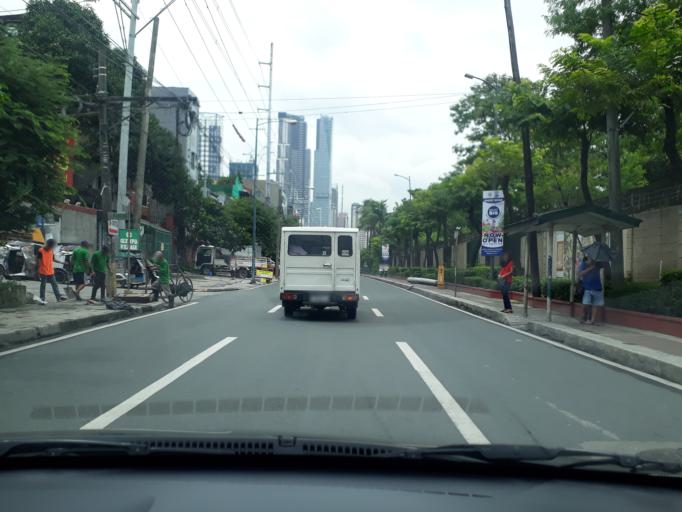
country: PH
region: Metro Manila
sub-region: Makati City
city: Makati City
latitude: 14.5684
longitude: 121.0183
